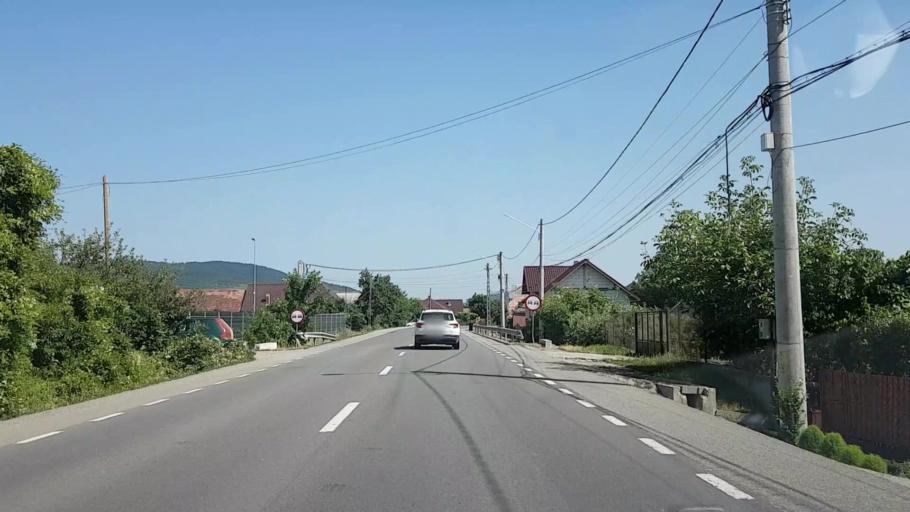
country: RO
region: Bistrita-Nasaud
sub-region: Comuna Sieu-Magherus
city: Sieu-Magherus
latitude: 47.0969
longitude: 24.3666
